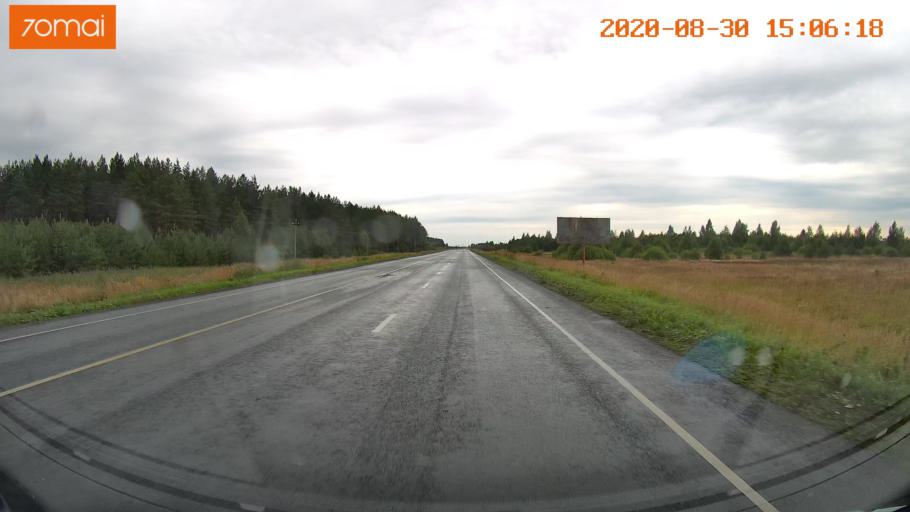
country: RU
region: Ivanovo
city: Staraya Vichuga
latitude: 57.2616
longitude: 41.9032
